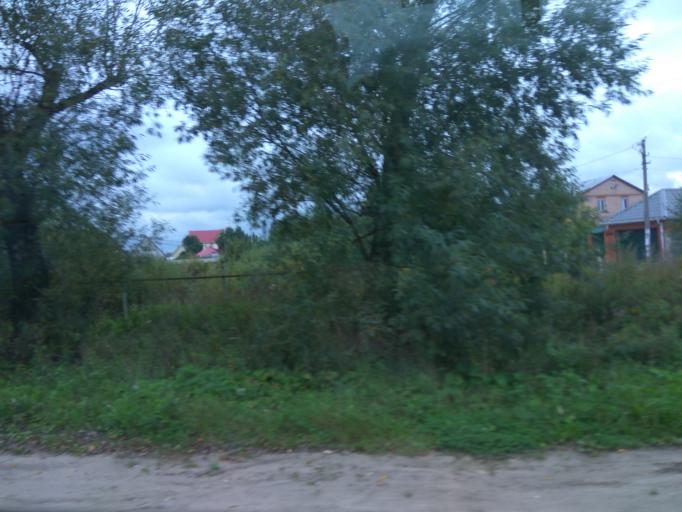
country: RU
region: Moskovskaya
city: Malyshevo
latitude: 55.5357
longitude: 38.3266
